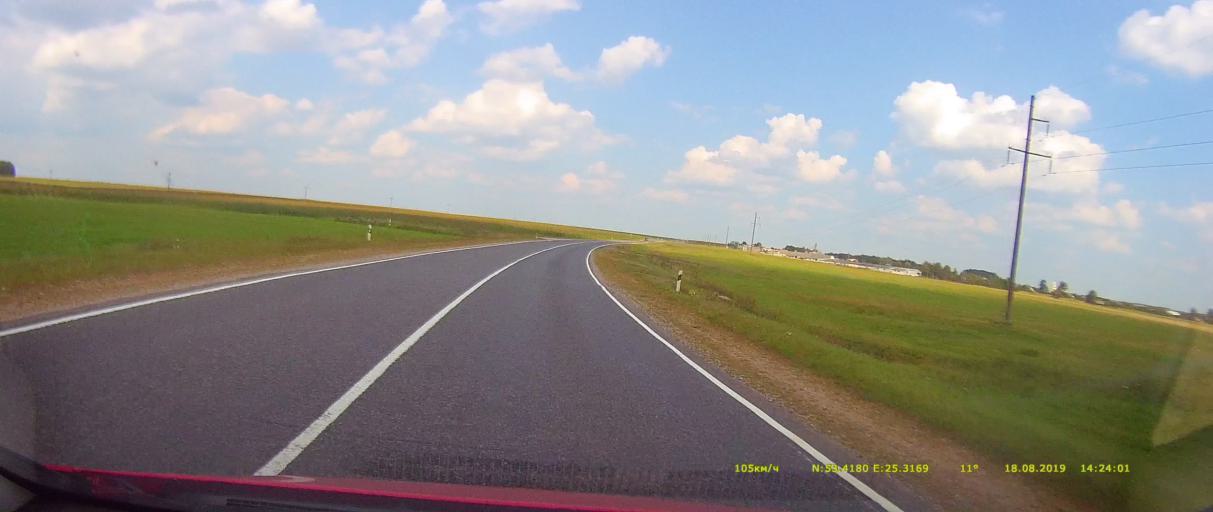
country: BY
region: Grodnenskaya
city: Dzyatlava
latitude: 53.4320
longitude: 25.3404
